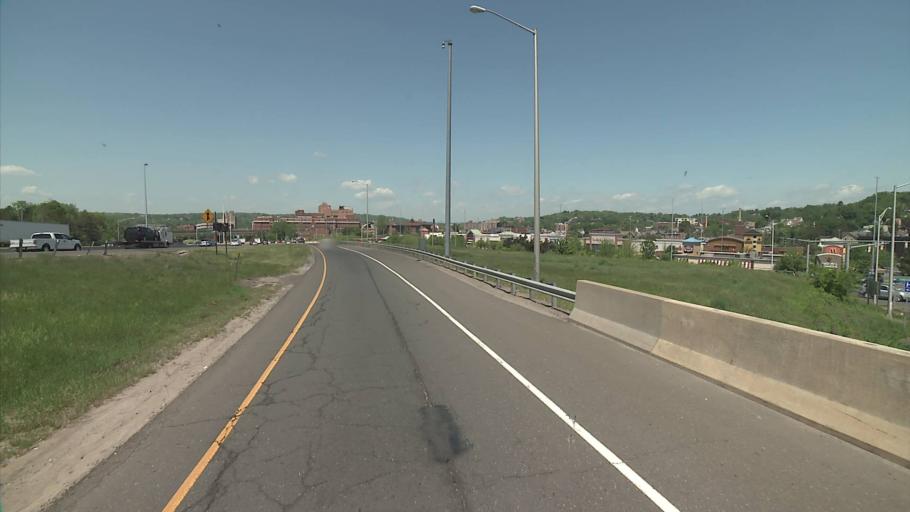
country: US
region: Connecticut
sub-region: New Haven County
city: Waterbury
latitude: 41.5512
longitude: -73.0303
